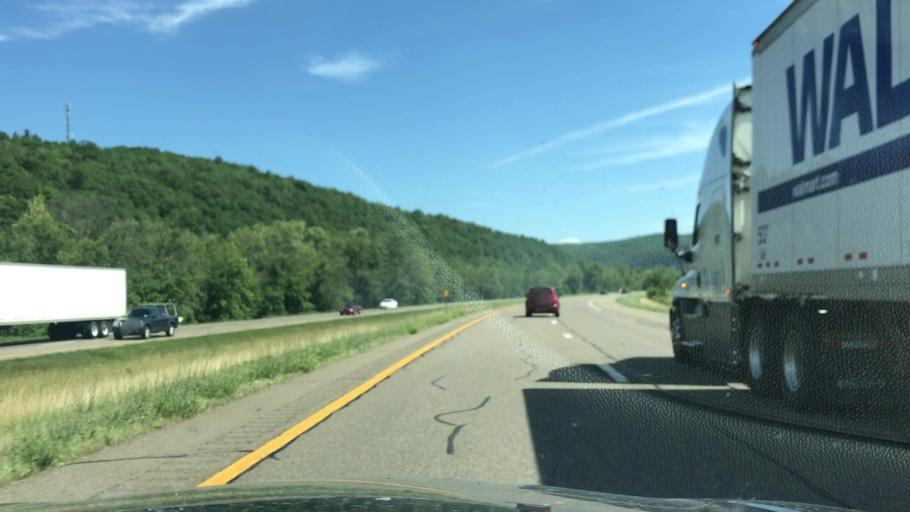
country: US
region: New York
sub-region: Steuben County
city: Gang Mills
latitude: 42.1992
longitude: -77.1631
